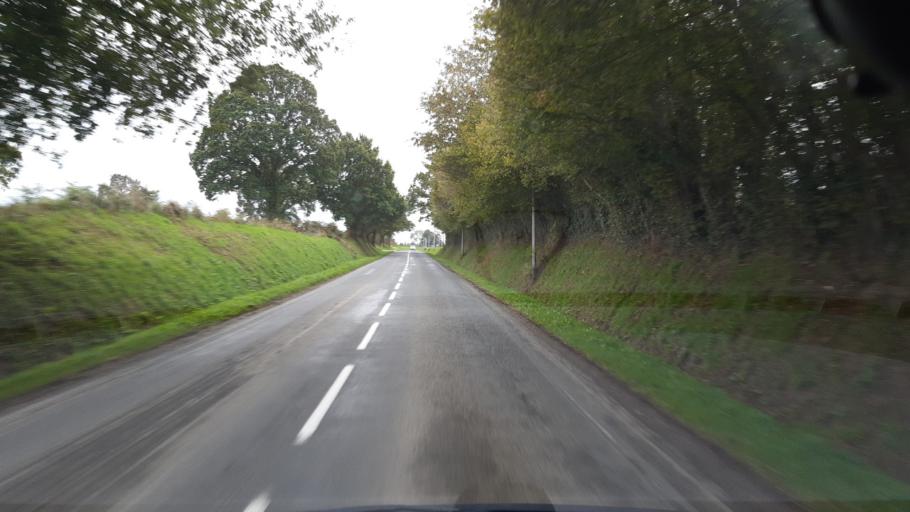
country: FR
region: Lower Normandy
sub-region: Departement de la Manche
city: Percy
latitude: 48.9951
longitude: -1.1998
